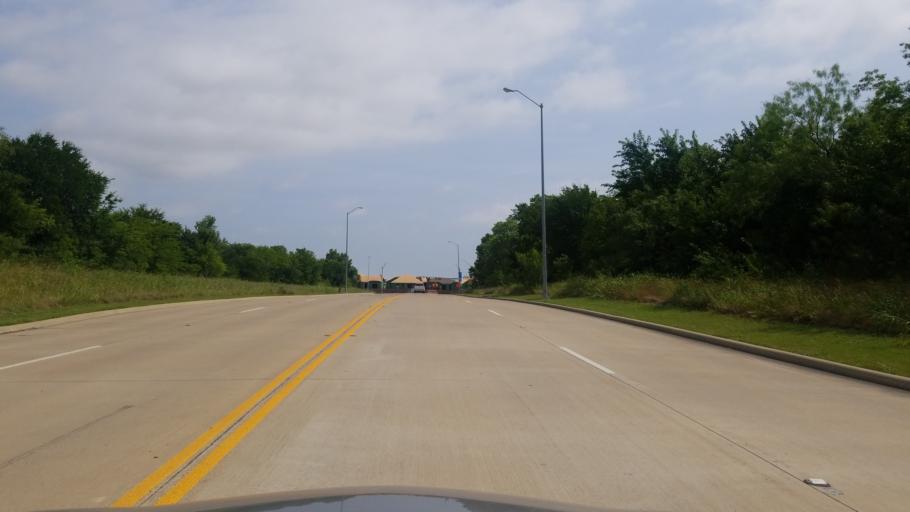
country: US
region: Texas
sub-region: Dallas County
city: Grand Prairie
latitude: 32.6799
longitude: -97.0296
